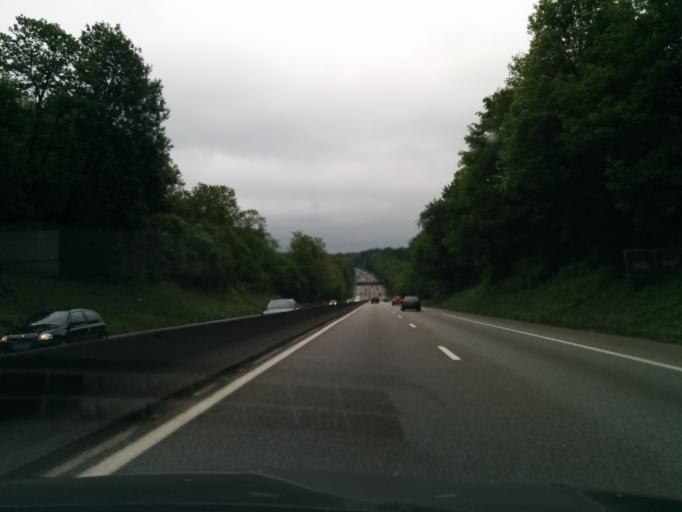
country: FR
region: Ile-de-France
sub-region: Departement des Yvelines
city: Chambourcy
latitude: 48.8971
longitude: 2.0063
